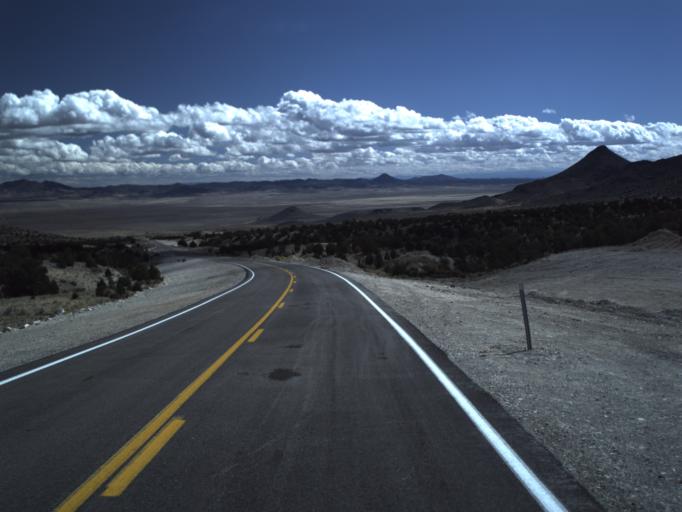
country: US
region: Utah
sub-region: Beaver County
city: Milford
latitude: 38.5115
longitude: -113.5248
